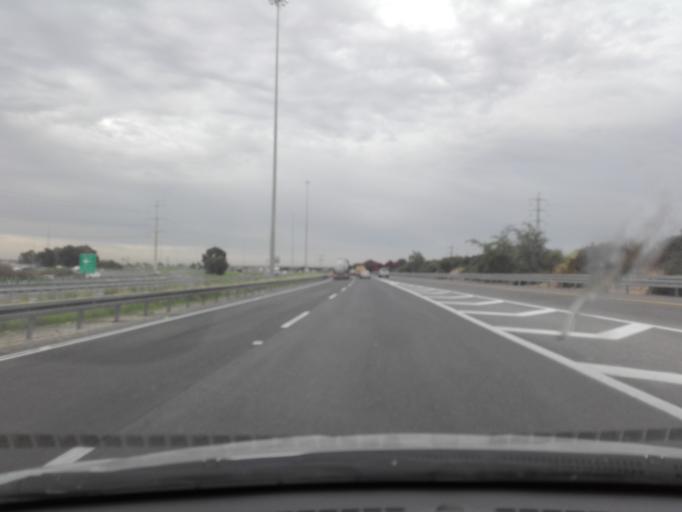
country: IL
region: Central District
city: Ramla
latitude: 31.9045
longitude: 34.8880
